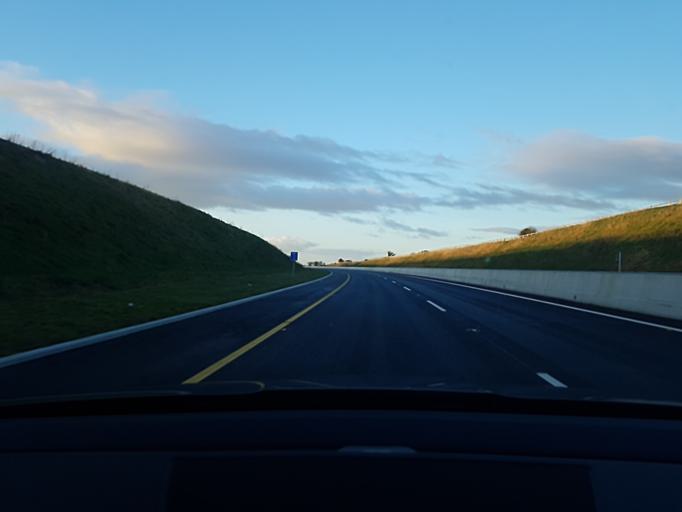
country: IE
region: Connaught
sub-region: County Galway
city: Athenry
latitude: 53.3657
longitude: -8.7879
